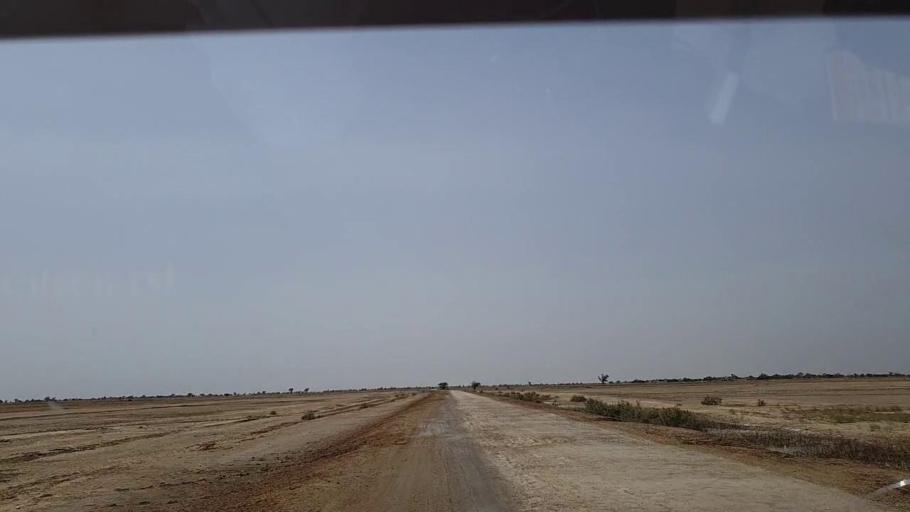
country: PK
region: Sindh
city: Johi
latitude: 26.7388
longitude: 67.6325
